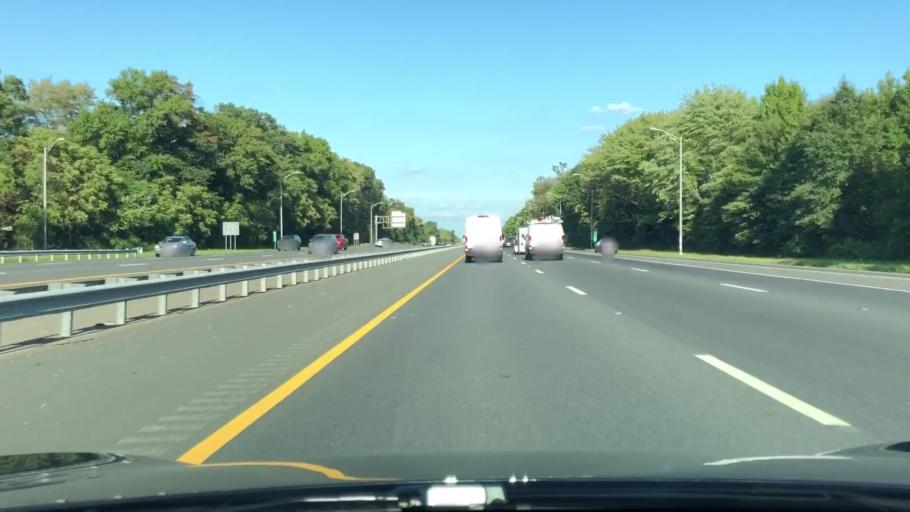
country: US
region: New Jersey
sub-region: Gloucester County
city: Paulsboro
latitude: 39.8298
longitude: -75.2193
